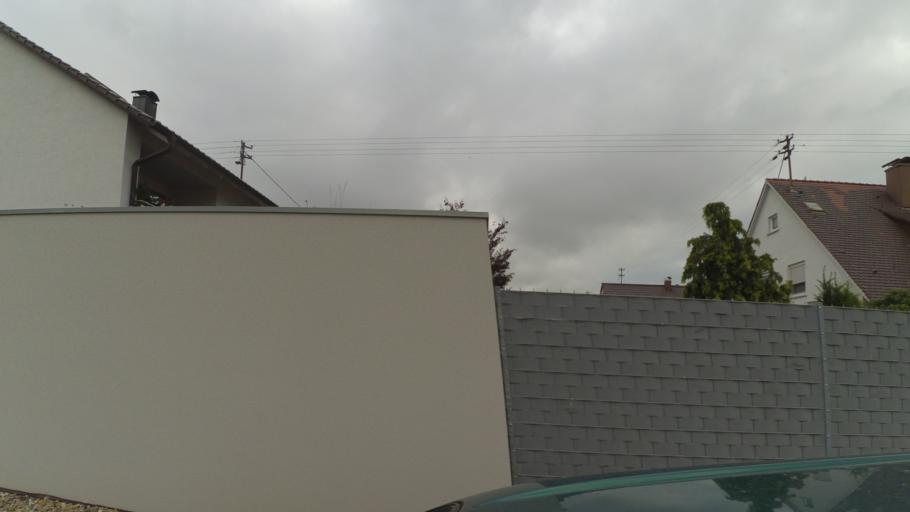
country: DE
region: Baden-Wuerttemberg
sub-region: Tuebingen Region
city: Langenau
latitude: 48.4882
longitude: 10.1127
